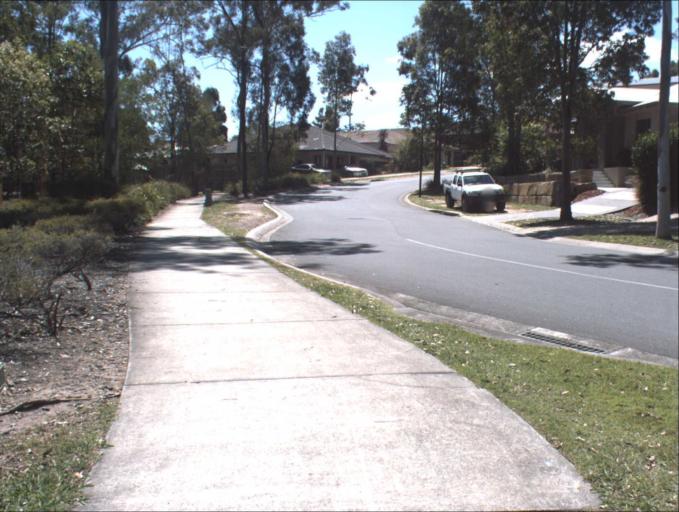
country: AU
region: Queensland
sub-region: Logan
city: Waterford West
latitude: -27.7101
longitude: 153.1566
